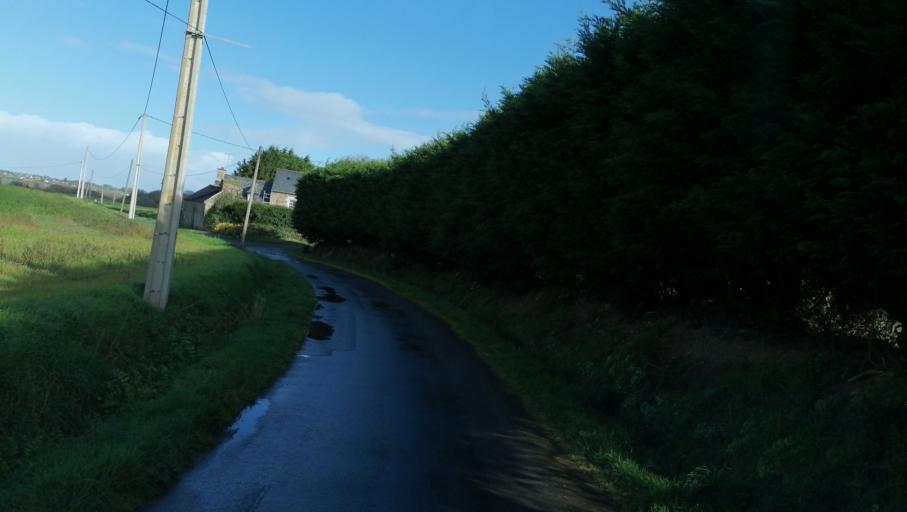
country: FR
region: Brittany
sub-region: Departement des Cotes-d'Armor
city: Plouha
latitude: 48.6566
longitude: -2.9026
